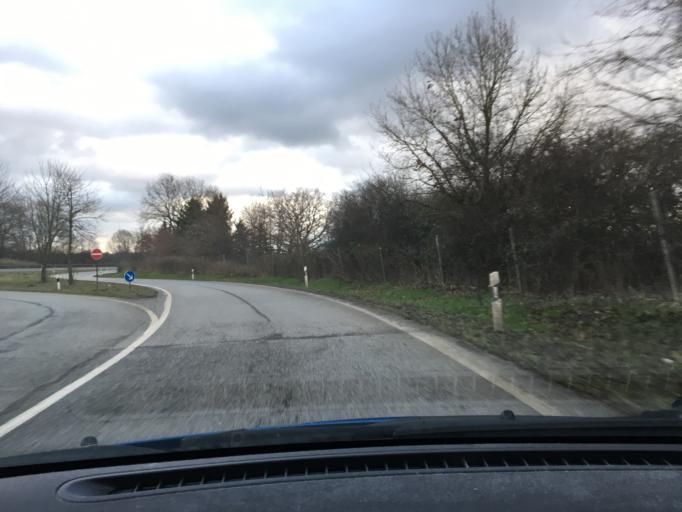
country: DE
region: Schleswig-Holstein
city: Neuenbrook
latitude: 53.8705
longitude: 9.5591
